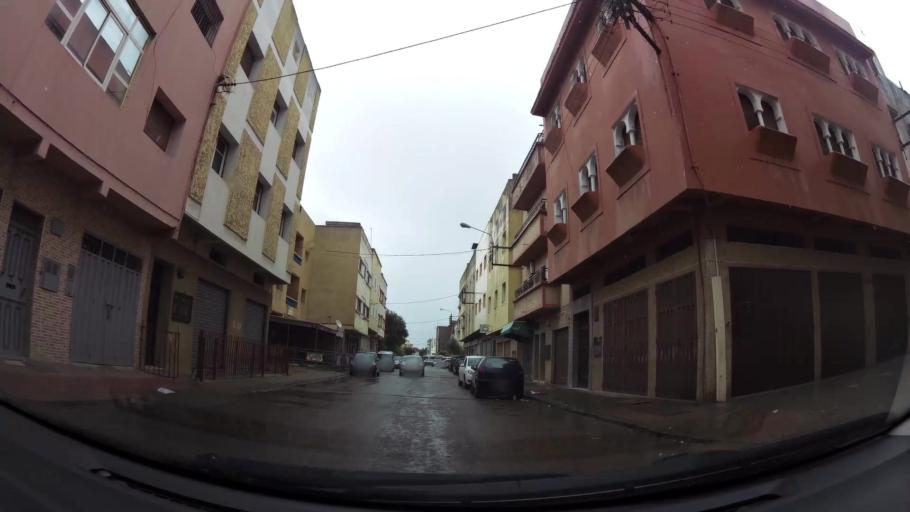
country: MA
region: Grand Casablanca
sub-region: Casablanca
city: Casablanca
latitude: 33.5503
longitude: -7.6813
